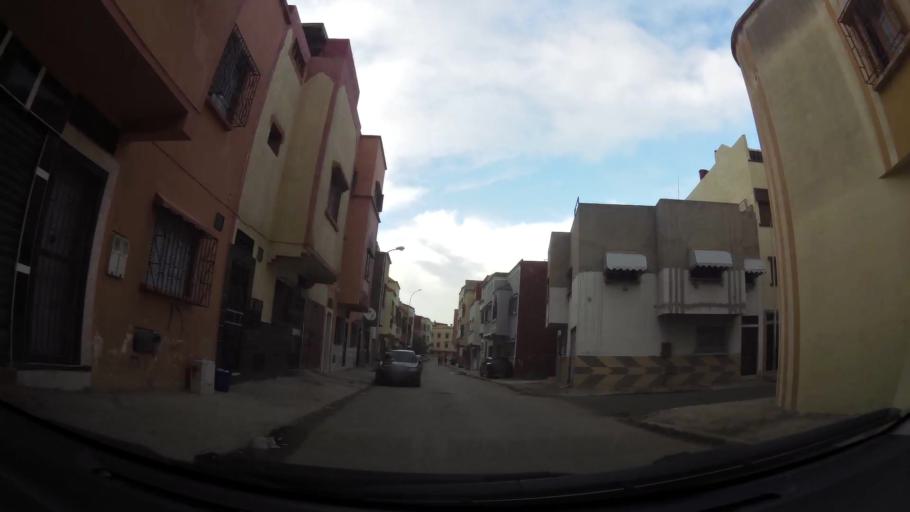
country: MA
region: Doukkala-Abda
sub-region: El-Jadida
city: El Jadida
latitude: 33.2490
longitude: -8.5276
